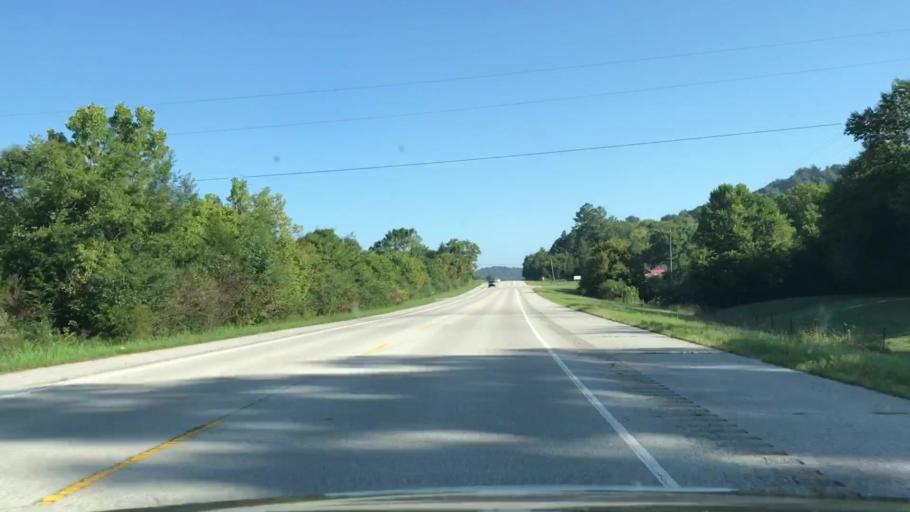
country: US
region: Tennessee
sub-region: Jackson County
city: Gainesboro
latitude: 36.4107
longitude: -85.6382
